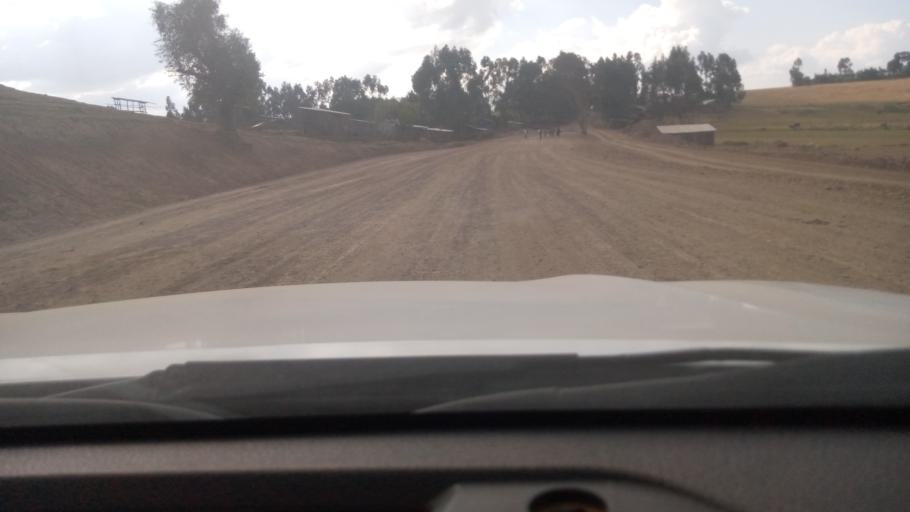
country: ET
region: Amhara
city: Debark'
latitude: 13.1569
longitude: 37.8275
